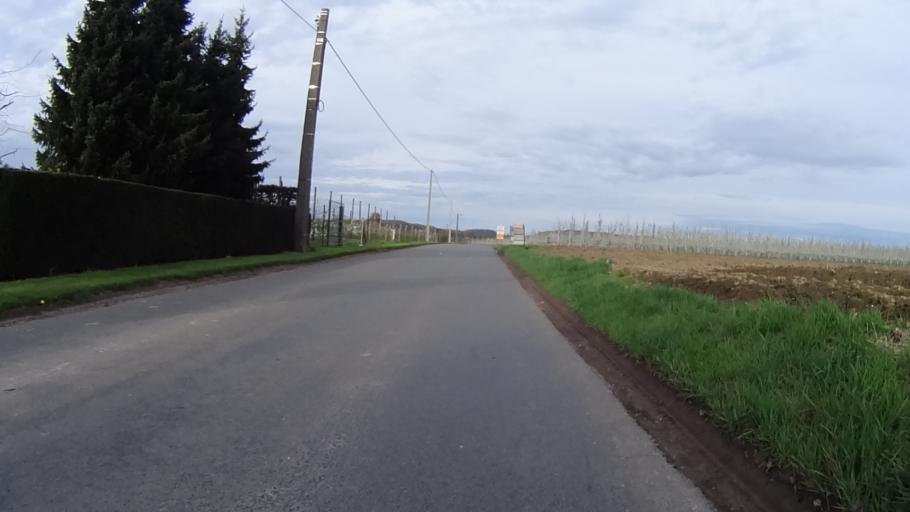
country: BE
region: Wallonia
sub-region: Province de Liege
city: Dalhem
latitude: 50.7482
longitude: 5.7455
